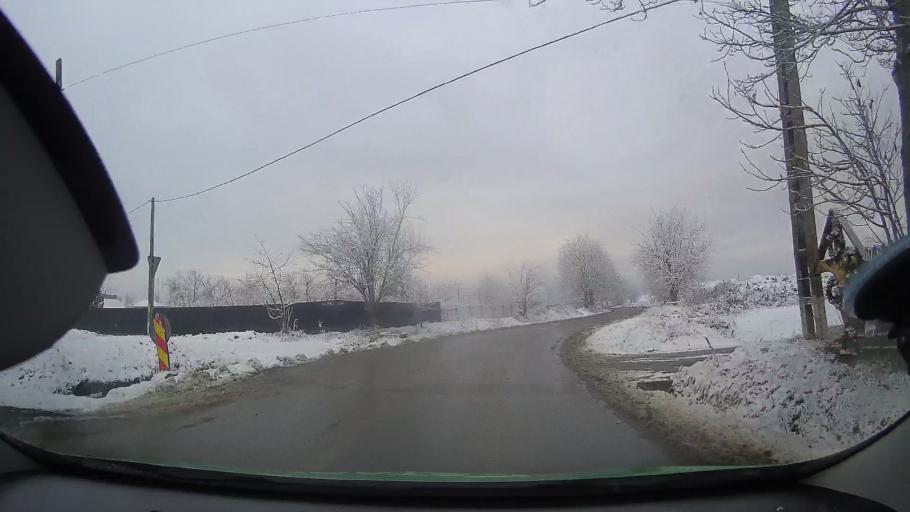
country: RO
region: Mures
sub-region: Comuna Bogata
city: Bogata
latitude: 46.4539
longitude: 24.0818
